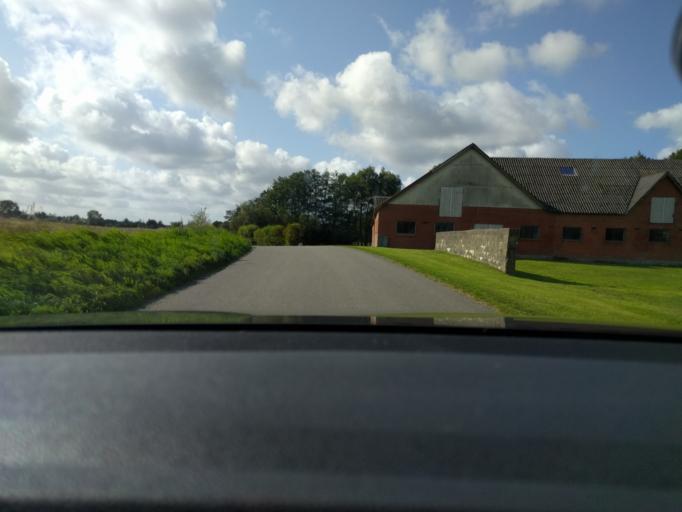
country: DK
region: Central Jutland
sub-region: Silkeborg Kommune
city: Silkeborg
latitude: 56.2660
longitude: 9.5566
